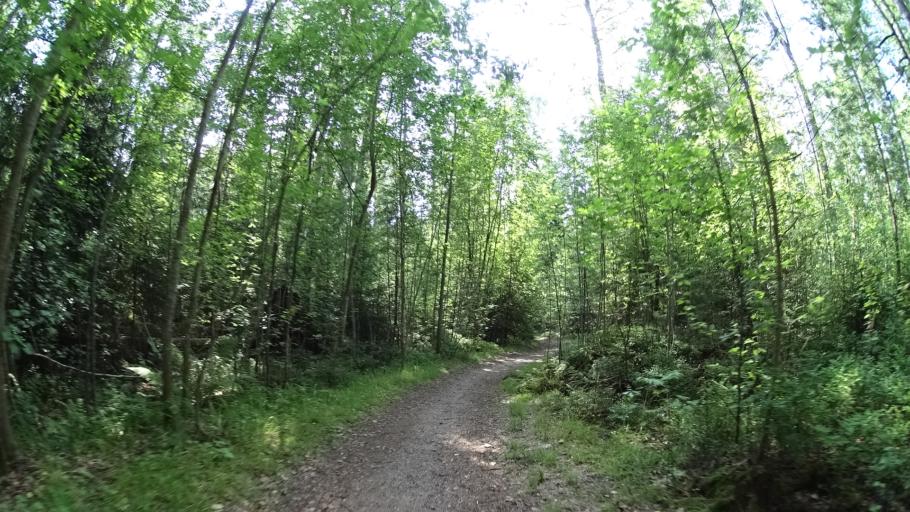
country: FI
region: Uusimaa
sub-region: Helsinki
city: Teekkarikylae
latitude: 60.2737
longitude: 24.9012
